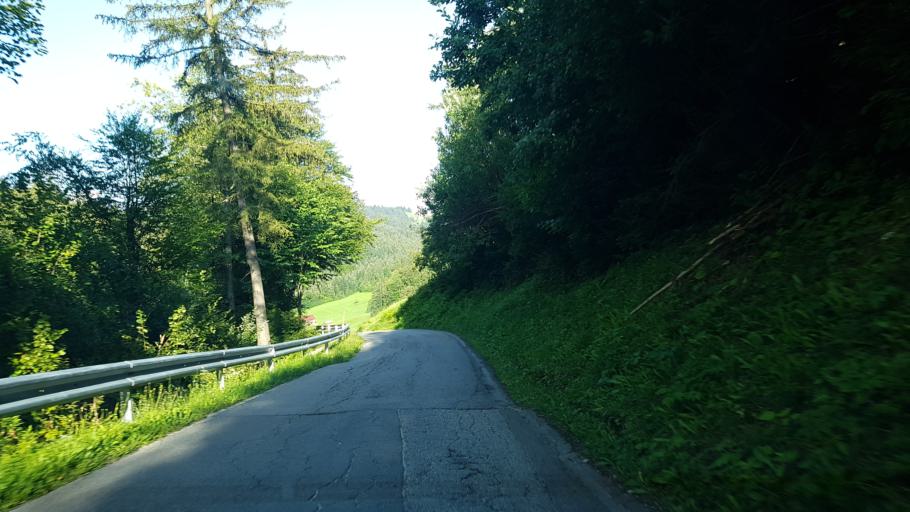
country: SI
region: Idrija
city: Spodnja Idrija
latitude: 46.0734
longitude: 14.0164
